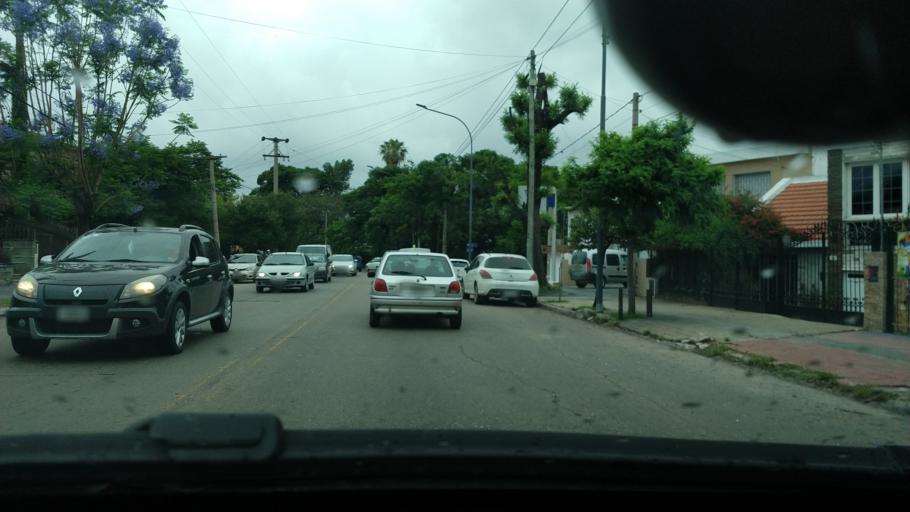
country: AR
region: Cordoba
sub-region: Departamento de Capital
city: Cordoba
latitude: -31.3866
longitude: -64.2271
